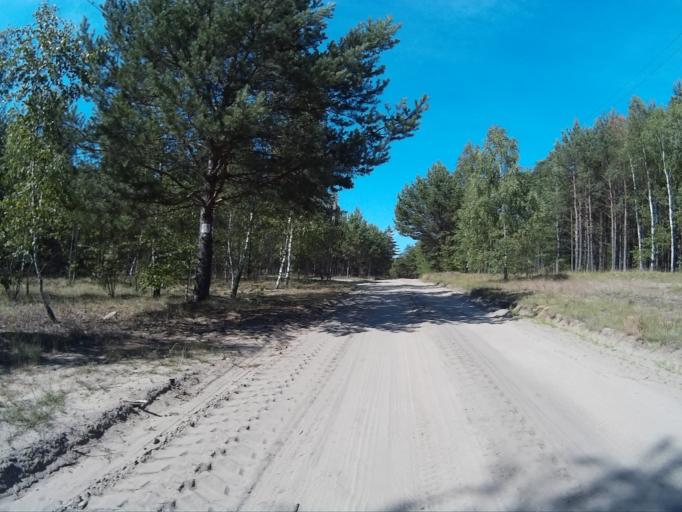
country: PL
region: Pomeranian Voivodeship
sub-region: Powiat chojnicki
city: Czersk
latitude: 53.7228
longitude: 17.9023
